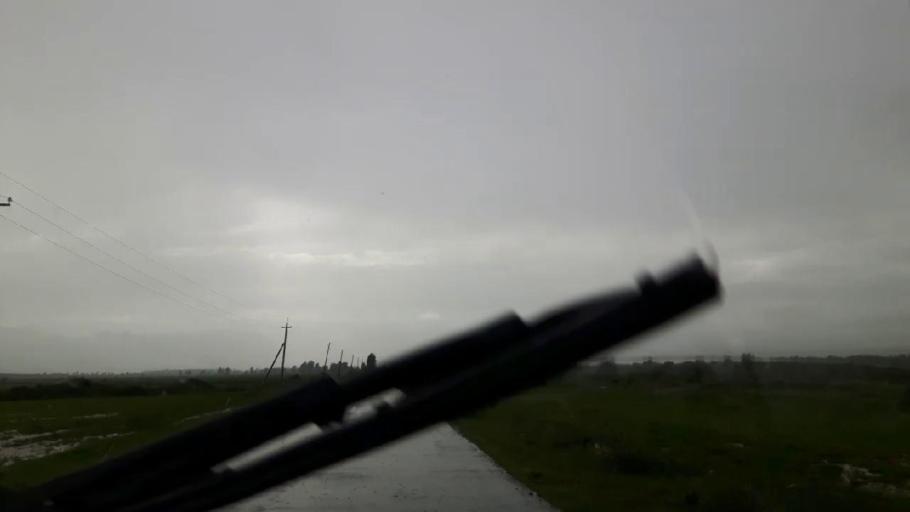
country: GE
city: Agara
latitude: 42.0149
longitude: 43.8157
